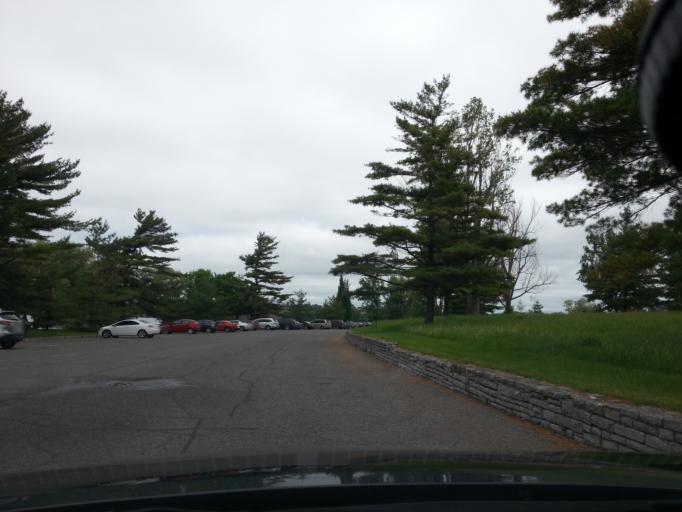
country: CA
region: Ontario
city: Ottawa
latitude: 45.4094
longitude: -75.7446
